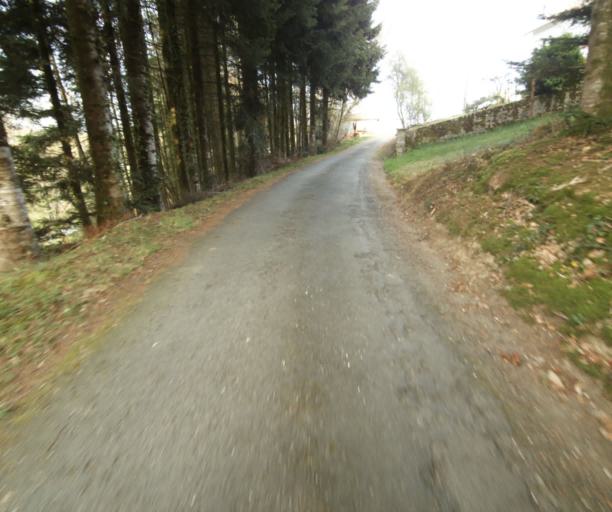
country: FR
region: Limousin
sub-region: Departement de la Correze
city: Naves
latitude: 45.3130
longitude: 1.7549
